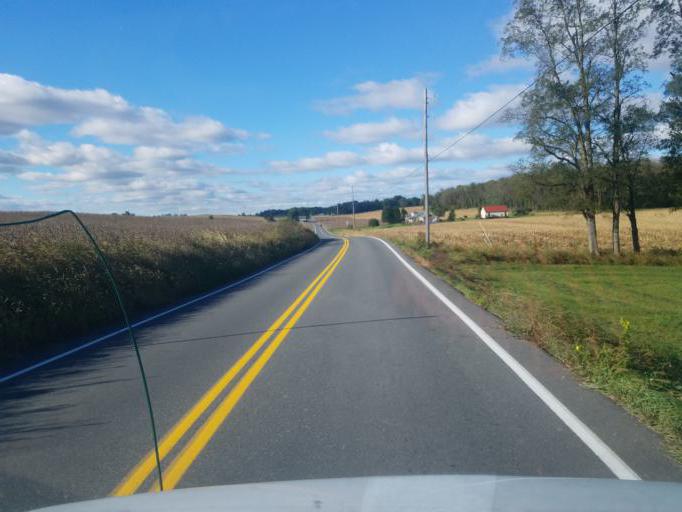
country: US
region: Pennsylvania
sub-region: Franklin County
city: Guilford Siding
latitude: 39.8478
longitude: -77.6117
